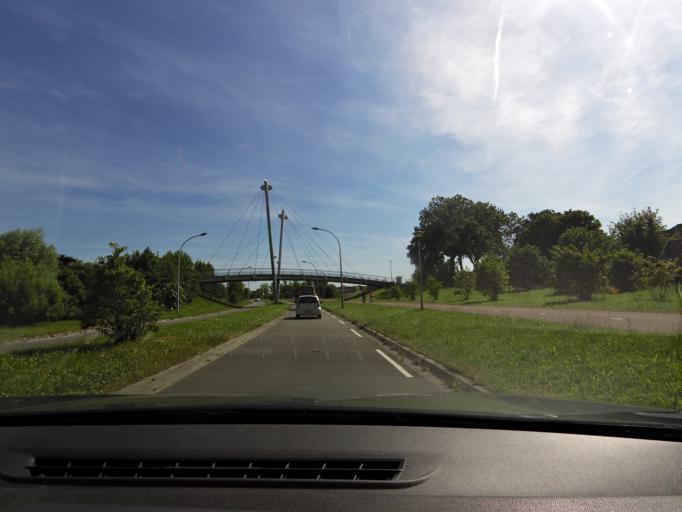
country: NL
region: South Holland
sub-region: Gemeente Barendrecht
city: Barendrecht
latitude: 51.8582
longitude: 4.5088
